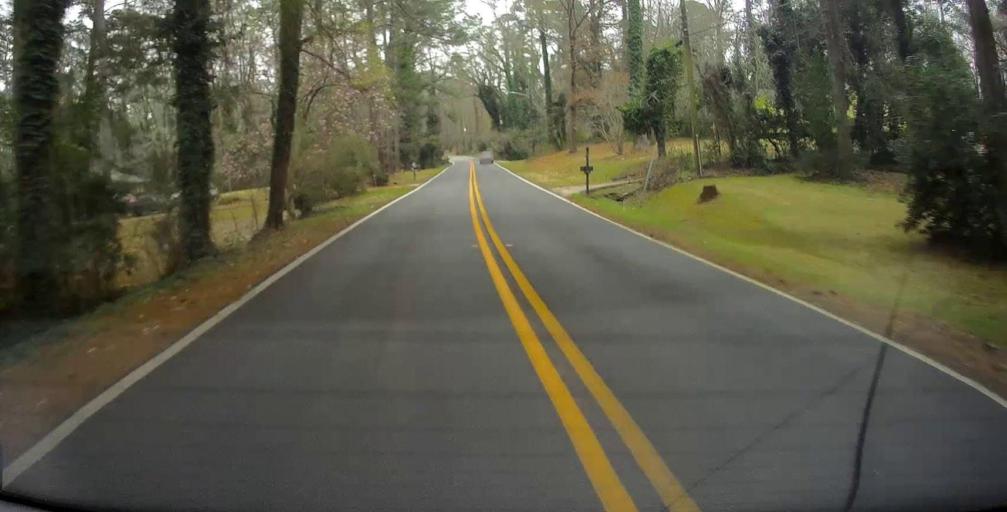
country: US
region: Georgia
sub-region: Bibb County
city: Macon
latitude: 32.8736
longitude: -83.7044
